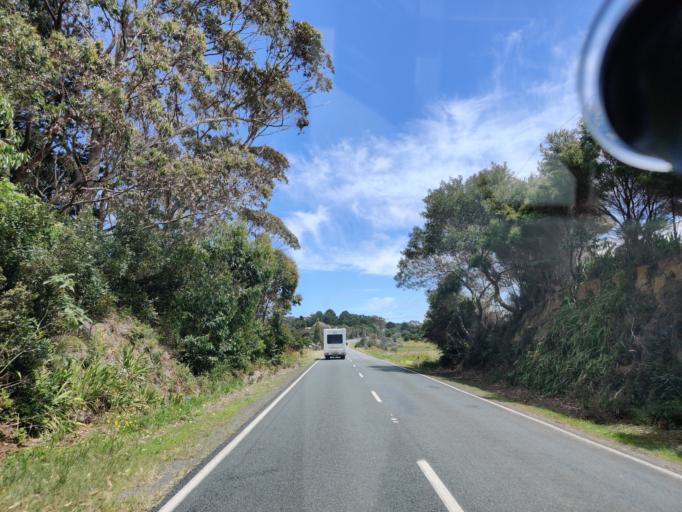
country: NZ
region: Northland
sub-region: Far North District
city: Kaitaia
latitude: -34.7481
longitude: 173.0532
